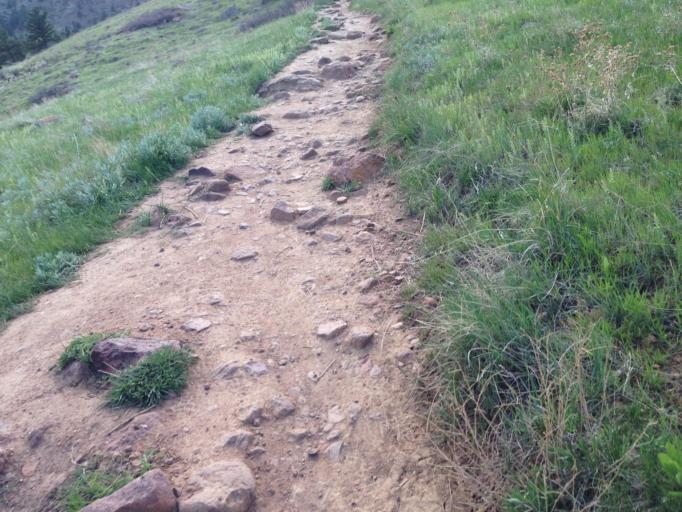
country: US
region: Colorado
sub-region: Boulder County
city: Boulder
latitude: 39.9398
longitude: -105.2647
